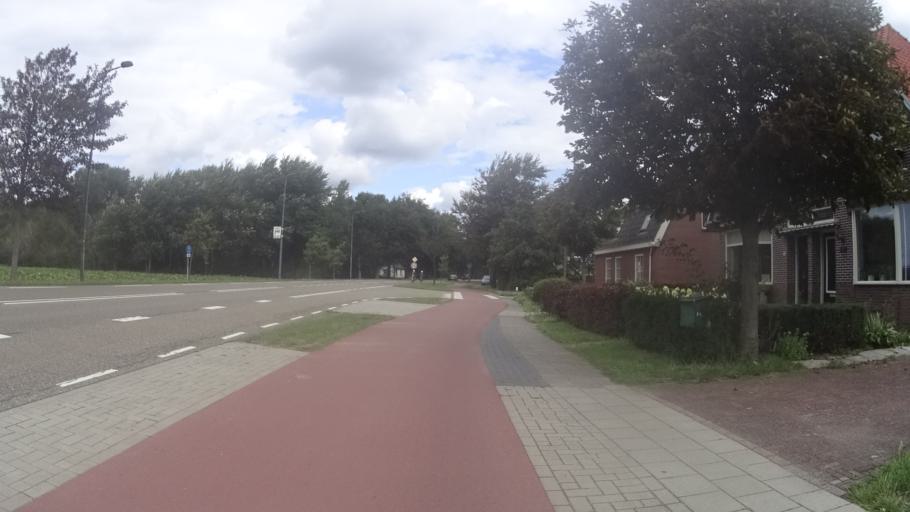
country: NL
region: North Holland
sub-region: Gemeente Heemskerk
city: Heemskerk
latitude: 52.5238
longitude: 4.6493
